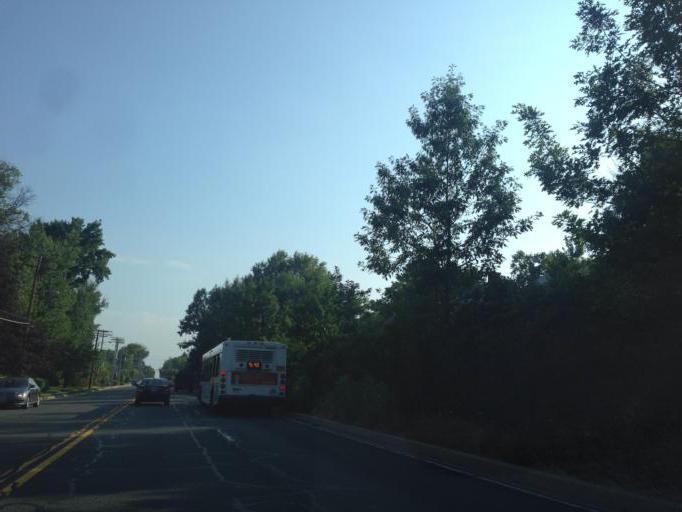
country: US
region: Maryland
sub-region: Baltimore County
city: Towson
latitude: 39.3813
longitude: -76.6077
